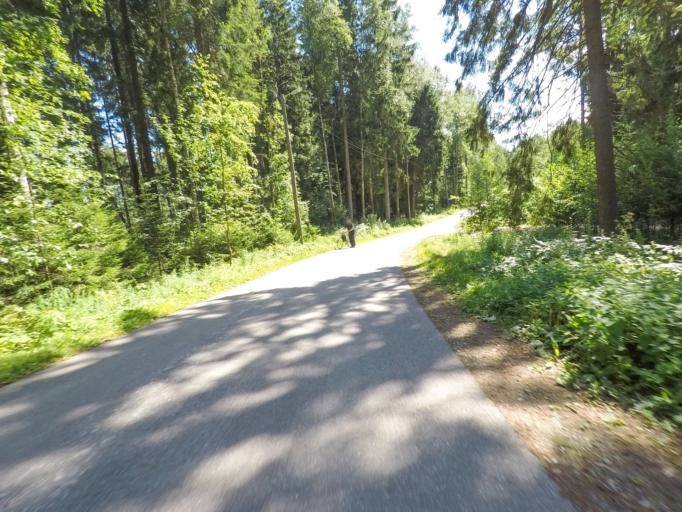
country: FI
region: Uusimaa
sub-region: Helsinki
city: Vantaa
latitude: 60.2171
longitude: 25.0693
